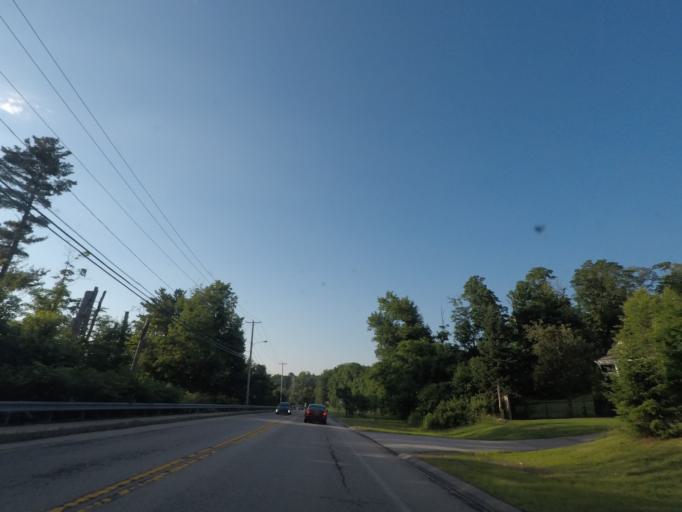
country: US
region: Massachusetts
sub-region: Worcester County
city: Sturbridge
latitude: 42.1028
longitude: -72.0757
